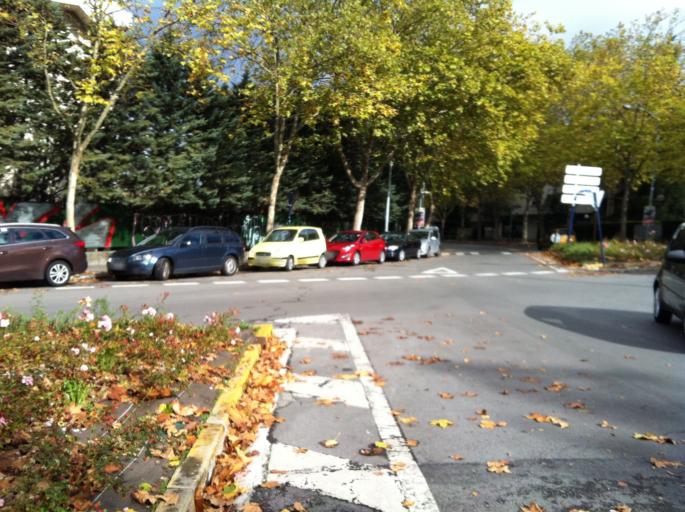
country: ES
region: Basque Country
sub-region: Provincia de Alava
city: Gasteiz / Vitoria
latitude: 42.8381
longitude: -2.6843
